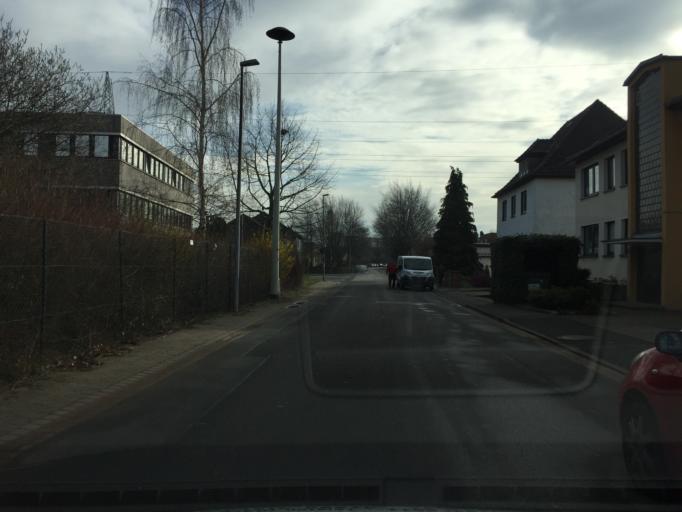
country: DE
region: Lower Saxony
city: Ronnenberg
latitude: 52.3427
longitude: 9.6574
